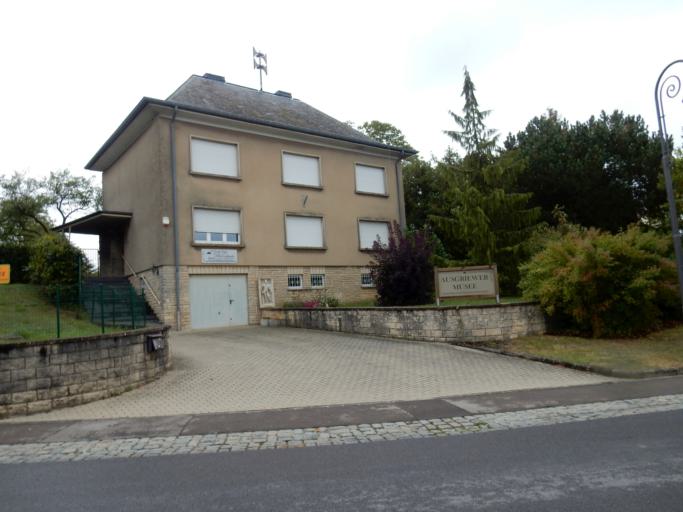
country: LU
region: Luxembourg
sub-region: Canton de Luxembourg
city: Olm
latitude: 49.6737
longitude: 6.0078
